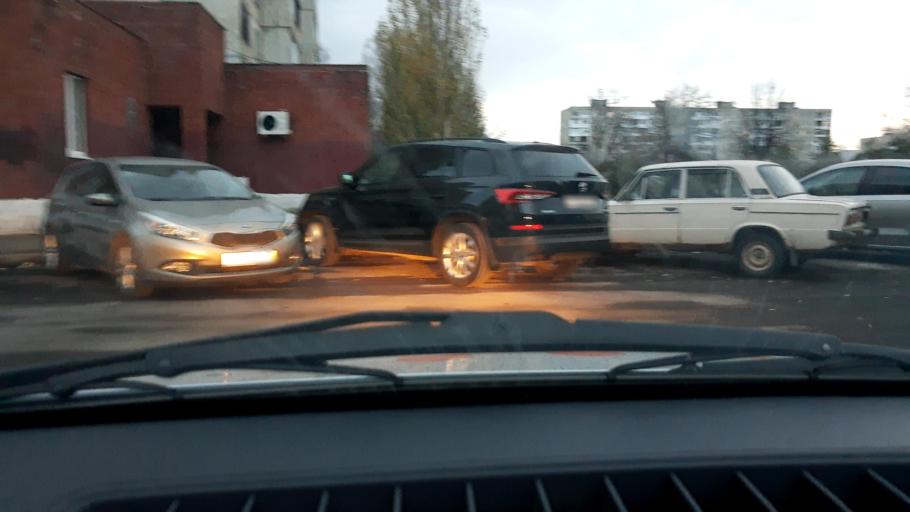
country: RU
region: Bashkortostan
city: Avdon
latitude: 54.7094
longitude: 55.8243
